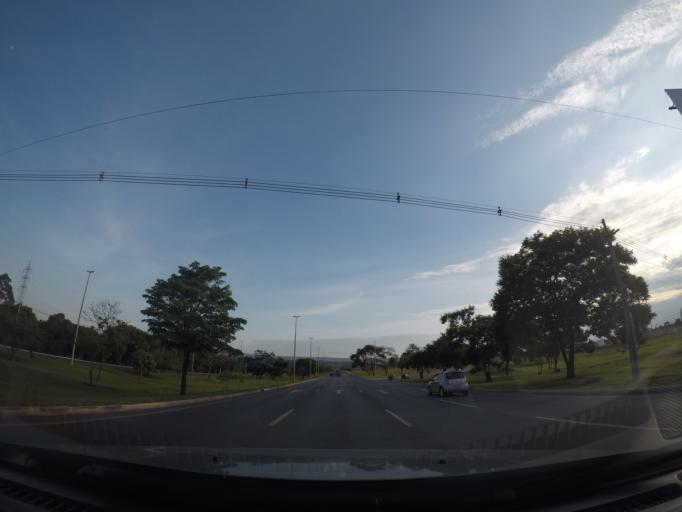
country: BR
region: Federal District
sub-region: Brasilia
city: Brasilia
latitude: -15.7401
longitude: -47.9167
